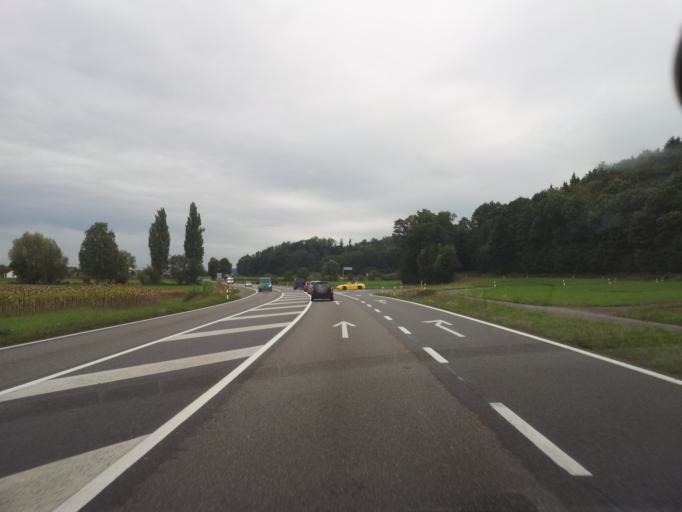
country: CH
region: Aargau
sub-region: Bezirk Lenzburg
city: Othmarsingen
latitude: 47.3827
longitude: 8.2140
